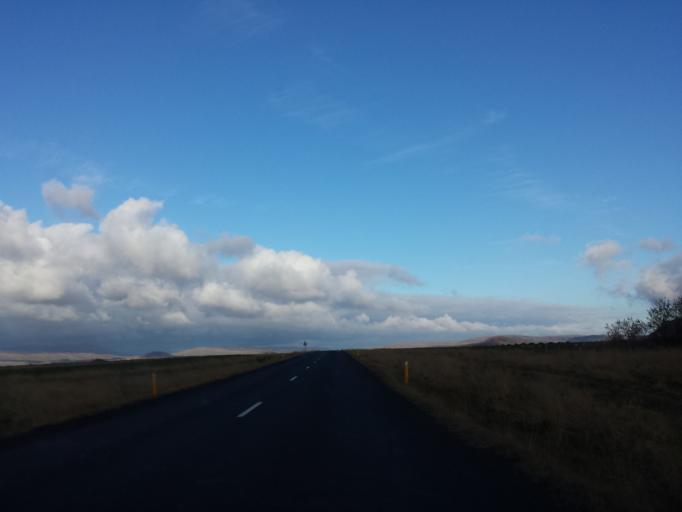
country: IS
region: West
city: Borgarnes
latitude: 64.8052
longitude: -22.2633
